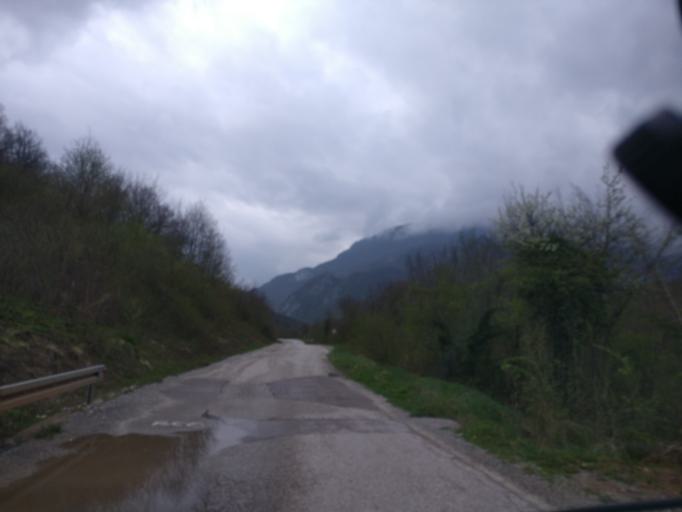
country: BA
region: Republika Srpska
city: Foca
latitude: 43.3518
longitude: 18.8283
